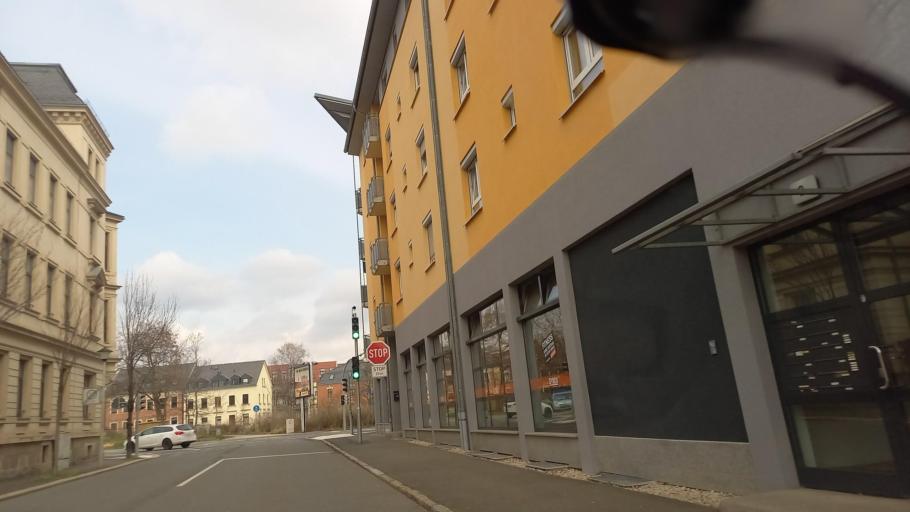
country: DE
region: Saxony
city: Zwickau
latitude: 50.7151
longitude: 12.4844
